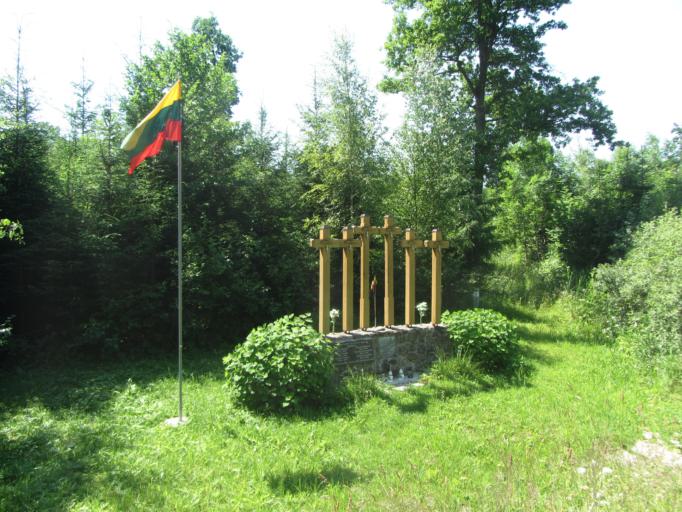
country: LT
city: Sirvintos
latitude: 55.2180
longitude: 24.9305
